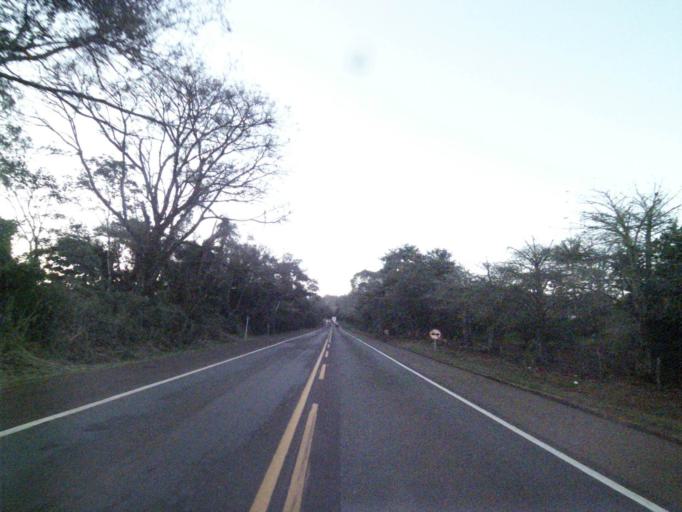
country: BR
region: Parana
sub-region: Londrina
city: Londrina
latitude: -23.4523
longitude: -51.1311
